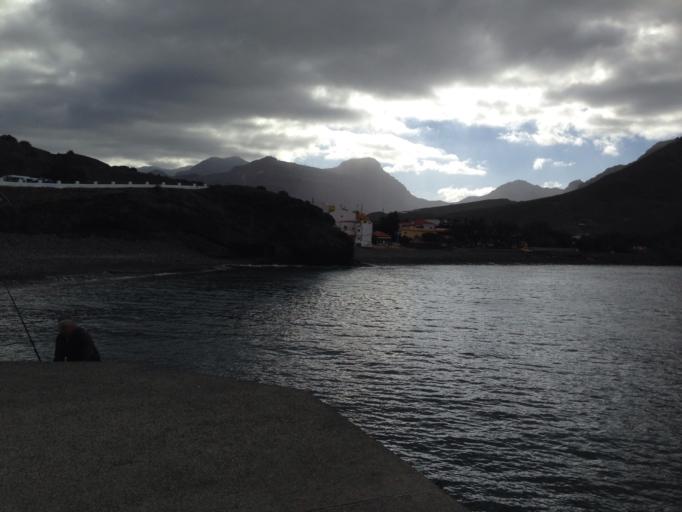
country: ES
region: Canary Islands
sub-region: Provincia de Las Palmas
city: San Nicolas
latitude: 28.0066
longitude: -15.8183
